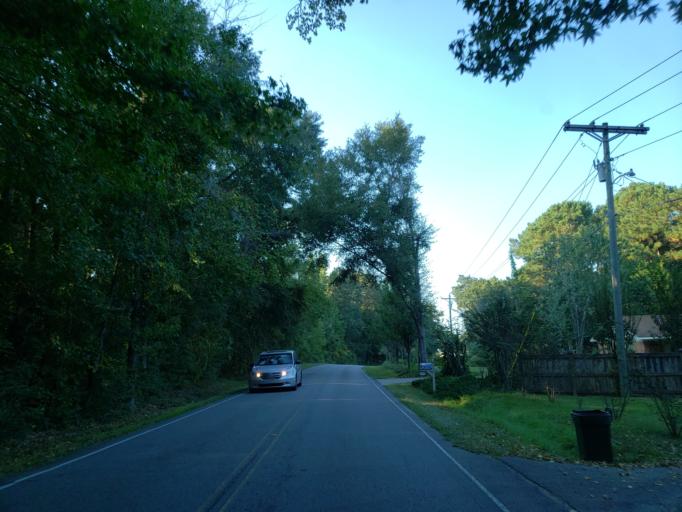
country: US
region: Mississippi
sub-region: Lamar County
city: West Hattiesburg
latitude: 31.3275
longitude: -89.4469
